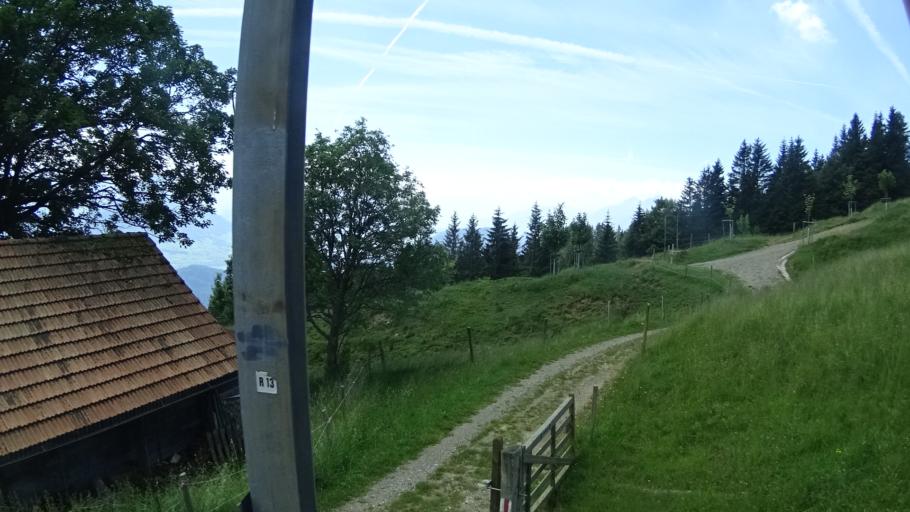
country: CH
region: Lucerne
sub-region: Lucerne-Land District
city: Vitznau
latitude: 47.0412
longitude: 8.4699
